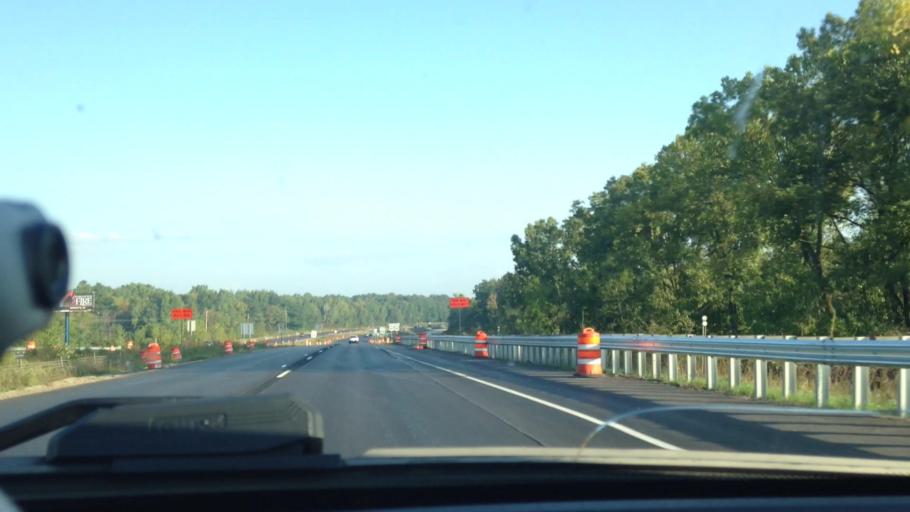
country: US
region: Wisconsin
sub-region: Brown County
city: Suamico
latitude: 44.6414
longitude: -88.0471
